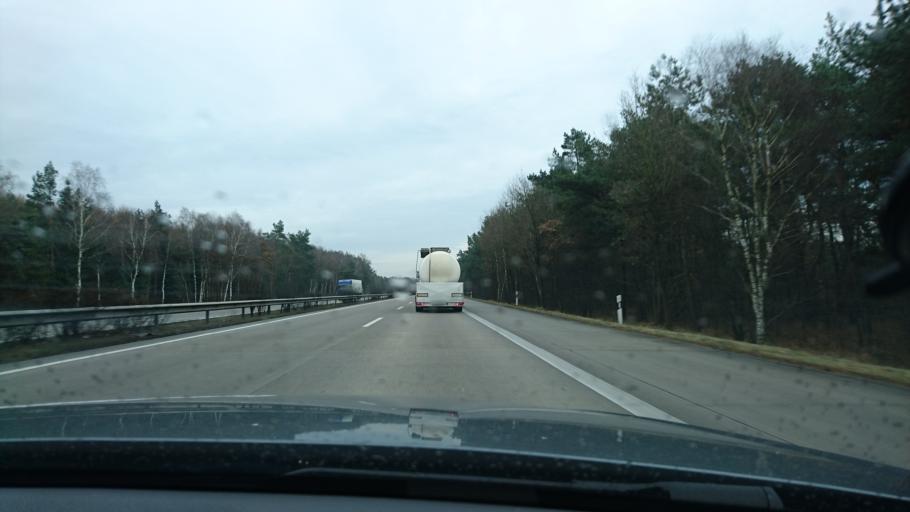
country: DE
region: Lower Saxony
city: Dotlingen
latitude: 52.9068
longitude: 8.3574
